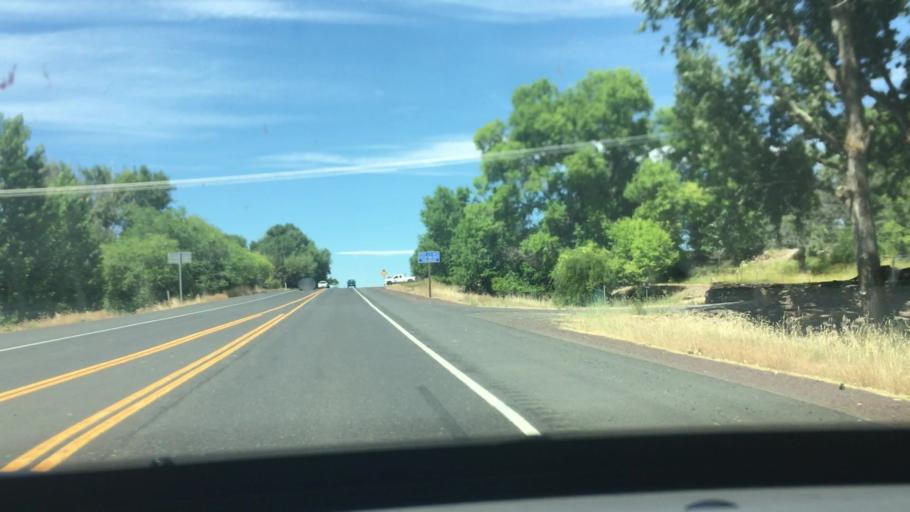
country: US
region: Oregon
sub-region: Deschutes County
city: Terrebonne
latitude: 44.3413
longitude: -121.1782
